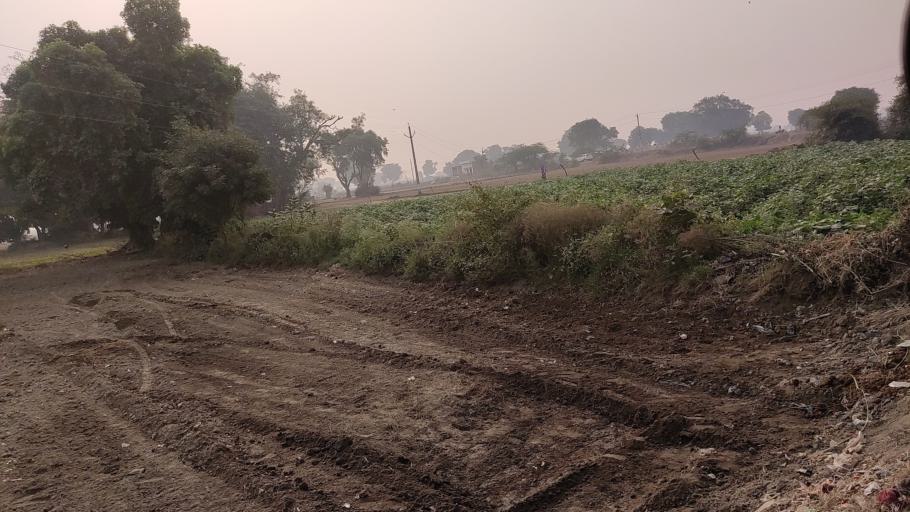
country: IN
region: Uttar Pradesh
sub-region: Mathura
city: Vrindavan
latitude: 27.5441
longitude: 77.7104
